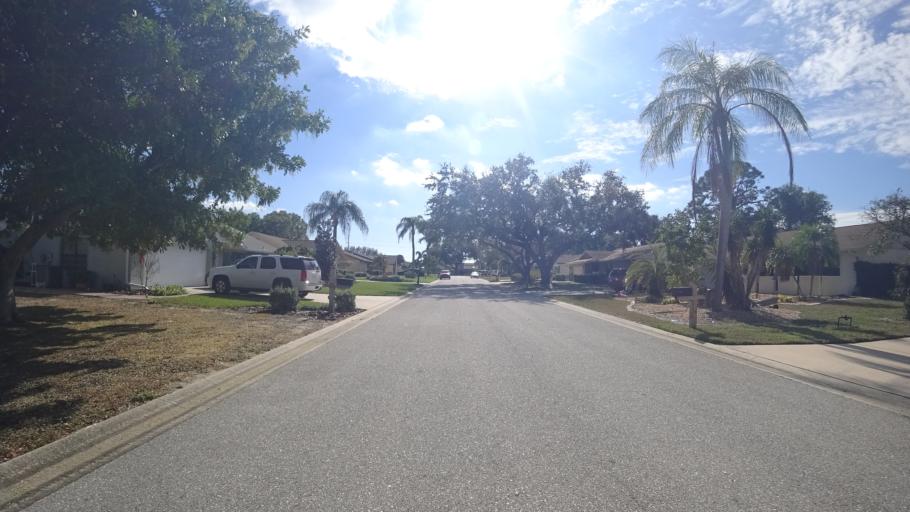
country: US
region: Florida
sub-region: Manatee County
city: West Bradenton
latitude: 27.5013
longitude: -82.6320
